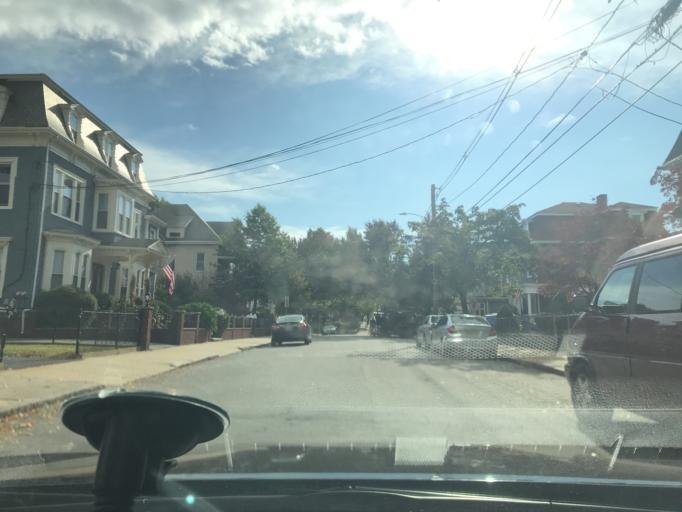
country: US
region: Massachusetts
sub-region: Middlesex County
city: Somerville
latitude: 42.3842
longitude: -71.0967
